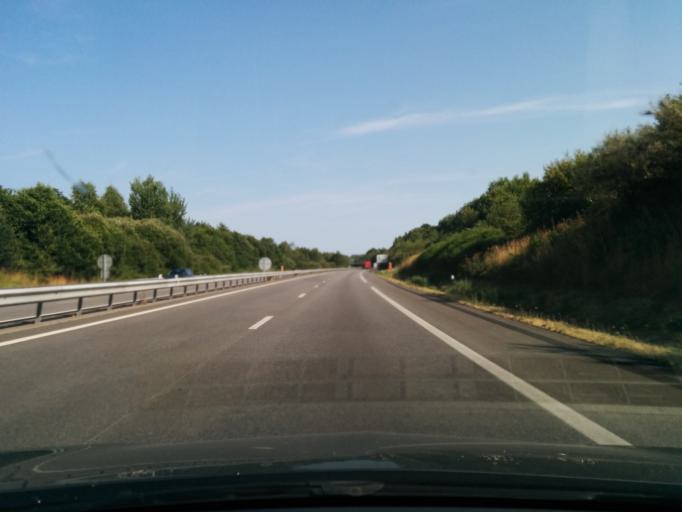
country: FR
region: Limousin
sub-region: Departement de la Haute-Vienne
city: Vicq-sur-Breuilh
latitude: 45.6398
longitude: 1.4208
